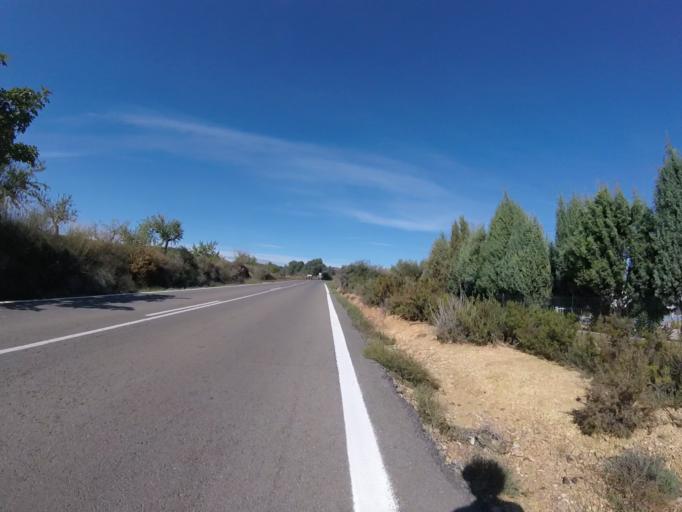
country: ES
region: Valencia
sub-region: Provincia de Castello
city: Benlloch
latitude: 40.2195
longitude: 0.0154
